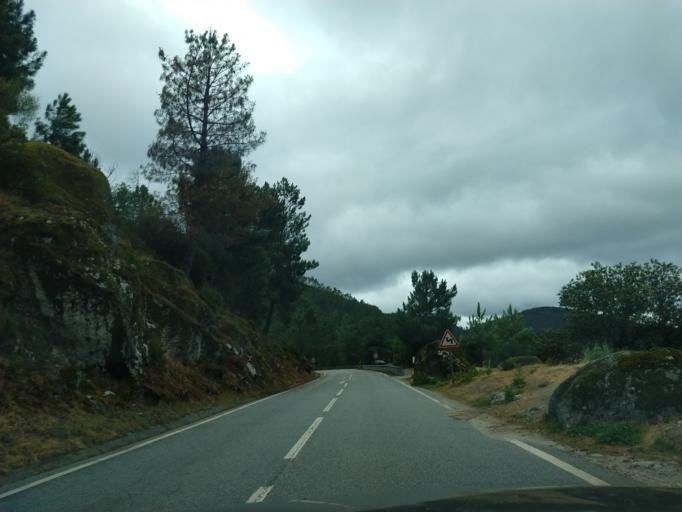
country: PT
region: Guarda
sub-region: Seia
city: Seia
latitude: 40.3263
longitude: -7.6790
